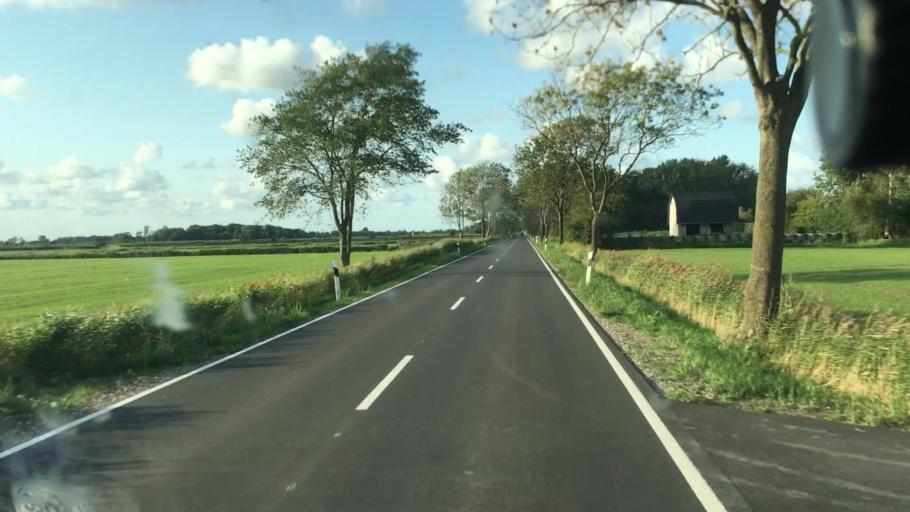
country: DE
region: Lower Saxony
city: Jever
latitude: 53.6297
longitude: 7.8616
